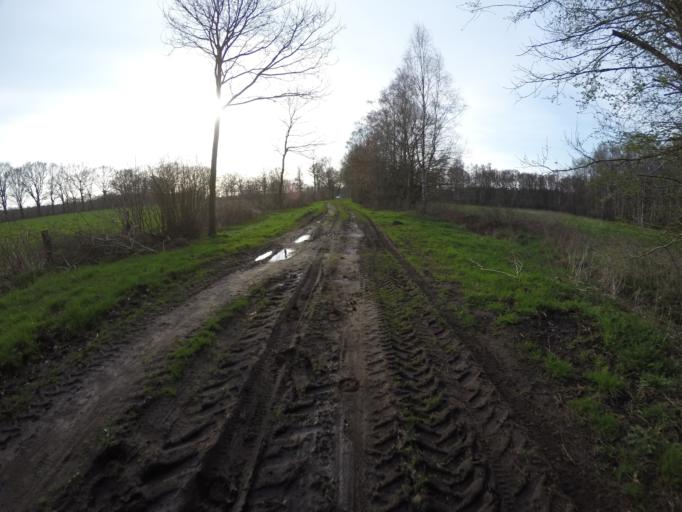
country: DE
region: Schleswig-Holstein
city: Hemdingen
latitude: 53.7282
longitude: 9.8409
